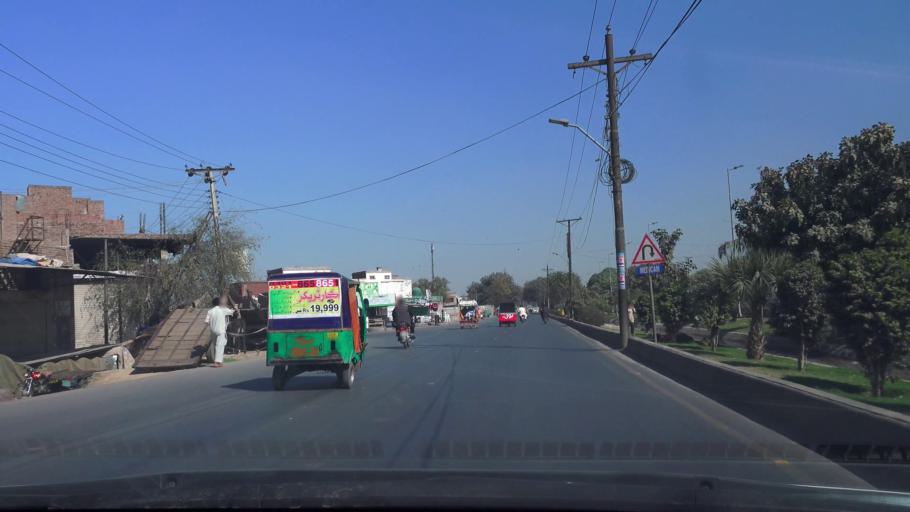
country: PK
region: Punjab
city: Faisalabad
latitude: 31.4143
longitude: 73.0781
